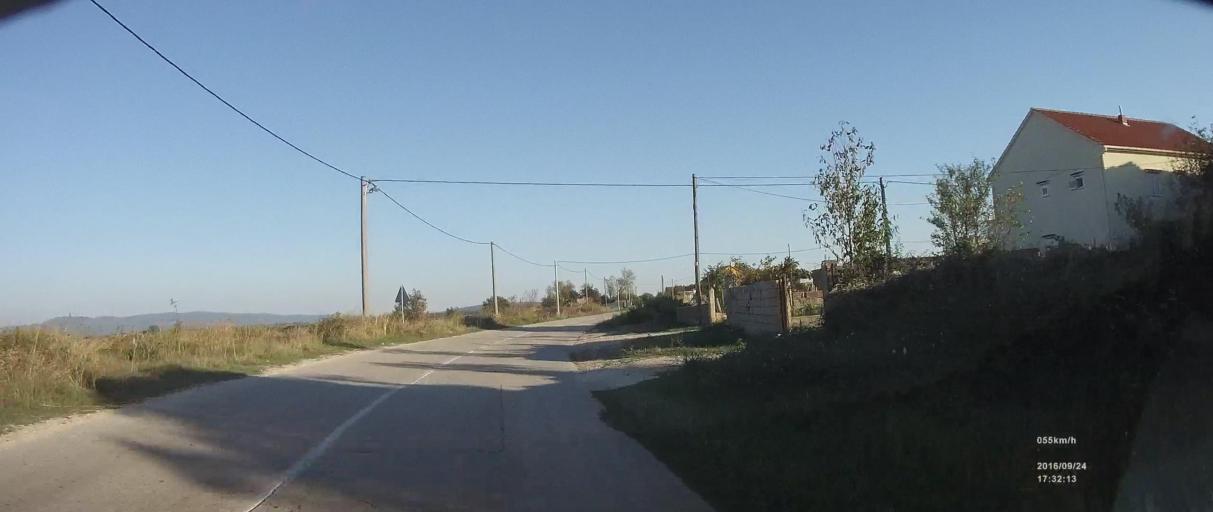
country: HR
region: Zadarska
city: Posedarje
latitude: 44.1838
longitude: 15.4487
